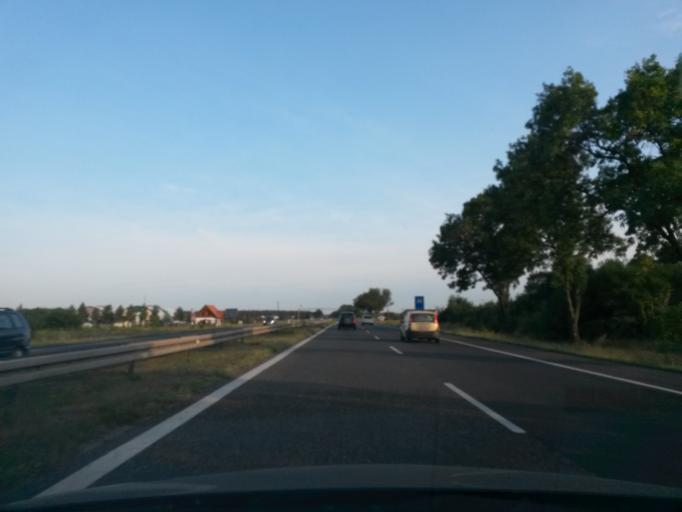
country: PL
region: Masovian Voivodeship
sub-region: Powiat plonski
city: Zaluski
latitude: 52.4711
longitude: 20.5681
